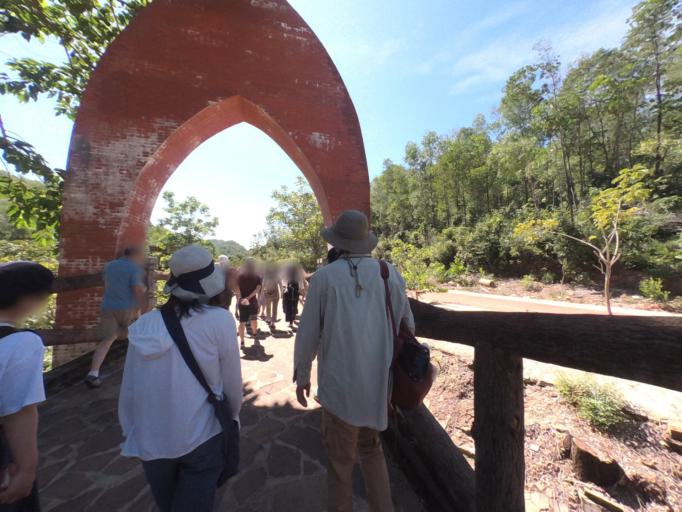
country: VN
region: Quang Nam
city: Dai Loc
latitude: 15.7721
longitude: 108.1102
